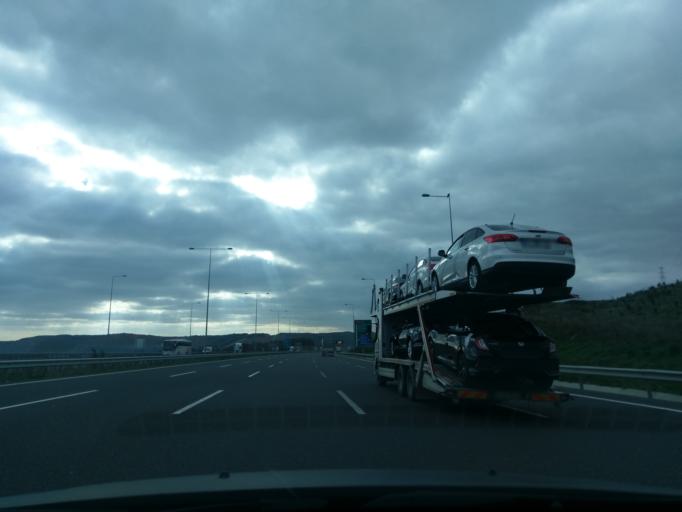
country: TR
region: Istanbul
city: Kemerburgaz
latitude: 41.2246
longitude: 28.8410
